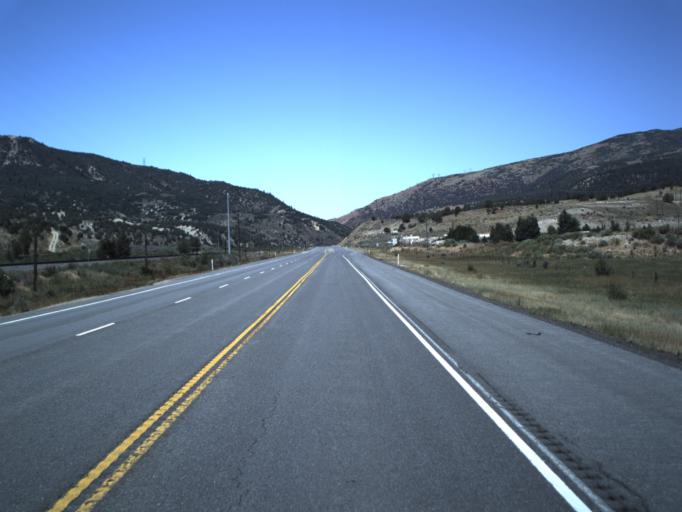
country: US
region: Utah
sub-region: Utah County
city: Mapleton
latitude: 39.9719
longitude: -111.3337
